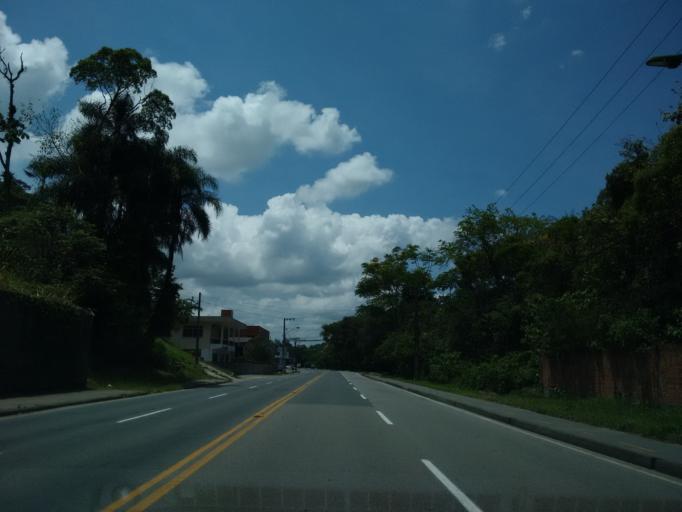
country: BR
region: Santa Catarina
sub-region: Blumenau
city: Blumenau
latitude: -26.9100
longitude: -49.0504
